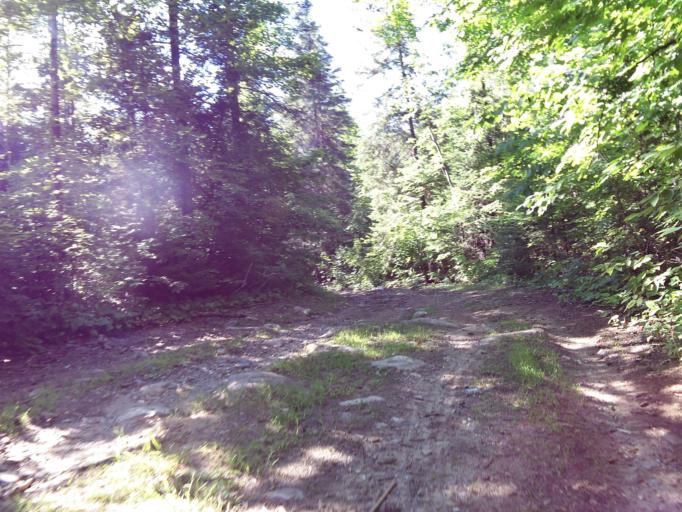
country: CA
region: Ontario
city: Renfrew
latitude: 45.1269
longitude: -76.7377
